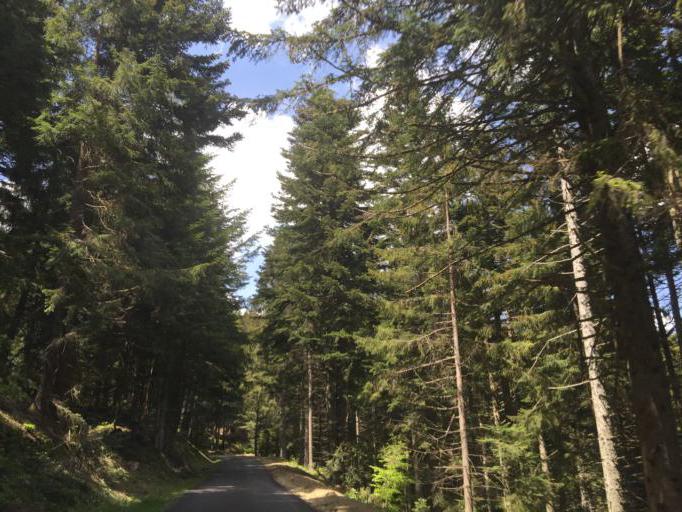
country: FR
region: Rhone-Alpes
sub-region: Departement de la Loire
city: Saint-Sauveur-en-Rue
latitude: 45.2812
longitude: 4.4711
